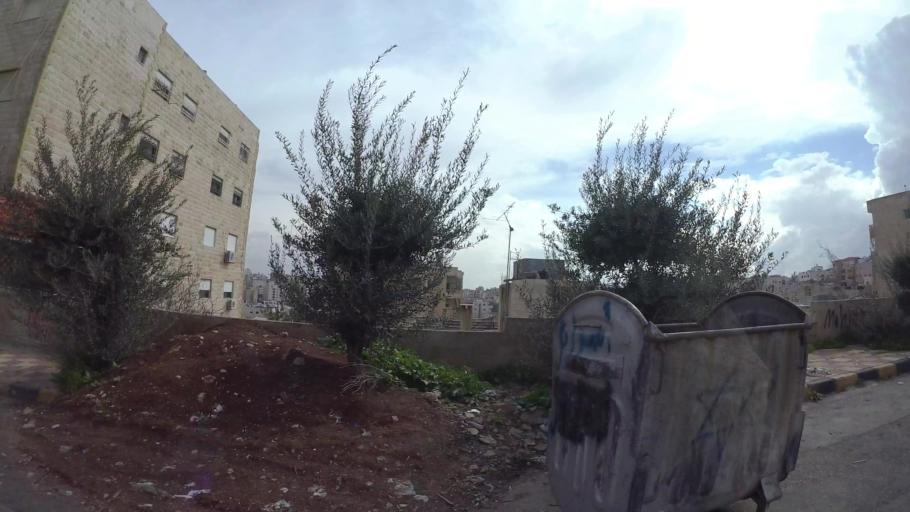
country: JO
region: Amman
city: Amman
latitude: 32.0101
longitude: 35.9387
